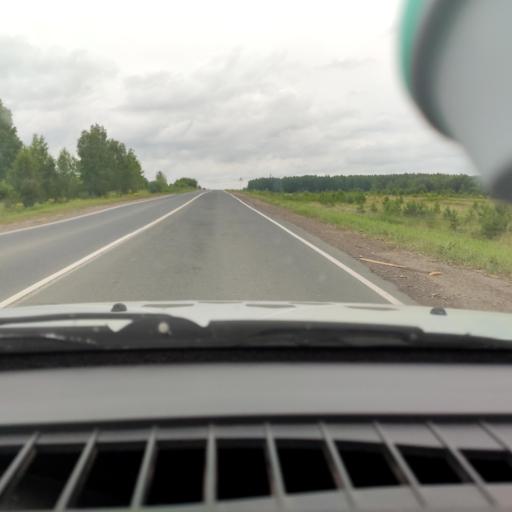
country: RU
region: Perm
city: Kungur
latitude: 57.4482
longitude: 56.9880
